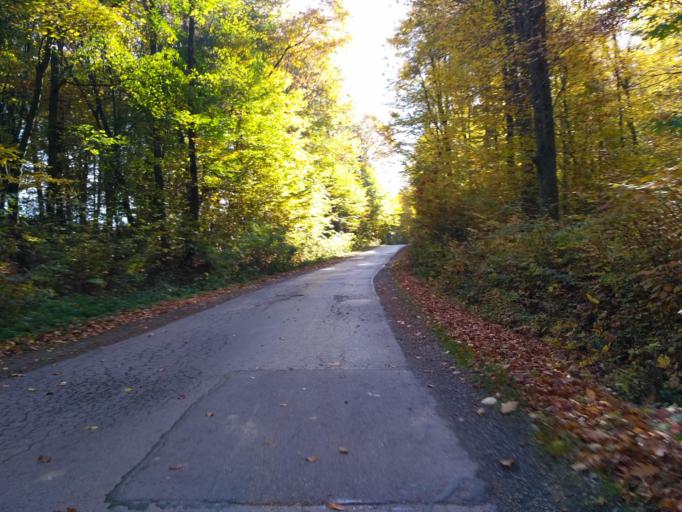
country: PL
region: Subcarpathian Voivodeship
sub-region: Powiat ropczycko-sedziszowski
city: Iwierzyce
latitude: 50.0439
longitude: 21.7741
